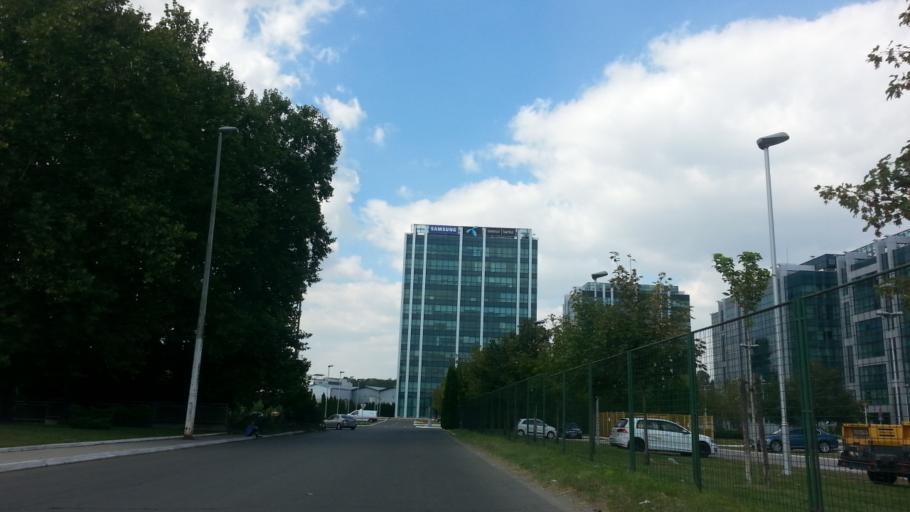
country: RS
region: Central Serbia
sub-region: Belgrade
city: Novi Beograd
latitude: 44.8111
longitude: 20.3976
